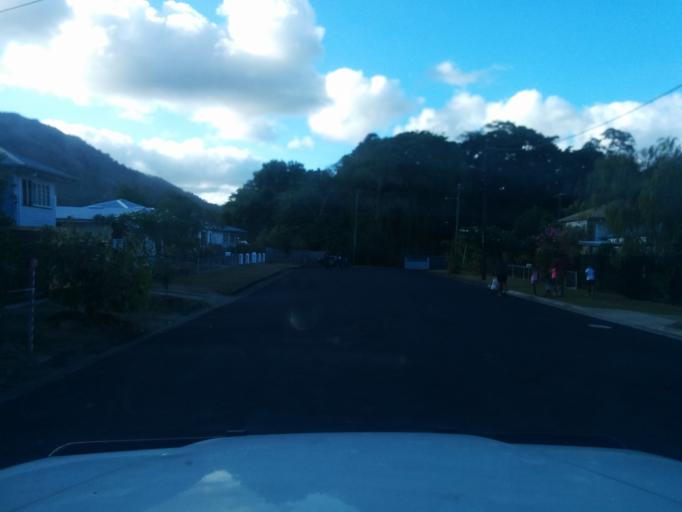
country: AU
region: Queensland
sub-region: Cairns
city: Woree
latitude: -16.9425
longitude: 145.7384
